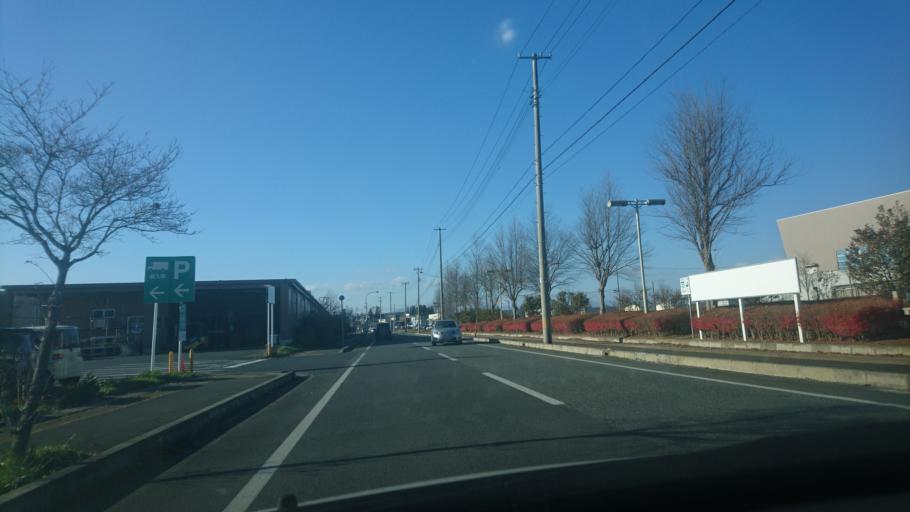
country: JP
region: Iwate
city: Ichinoseki
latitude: 38.9394
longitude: 141.1555
